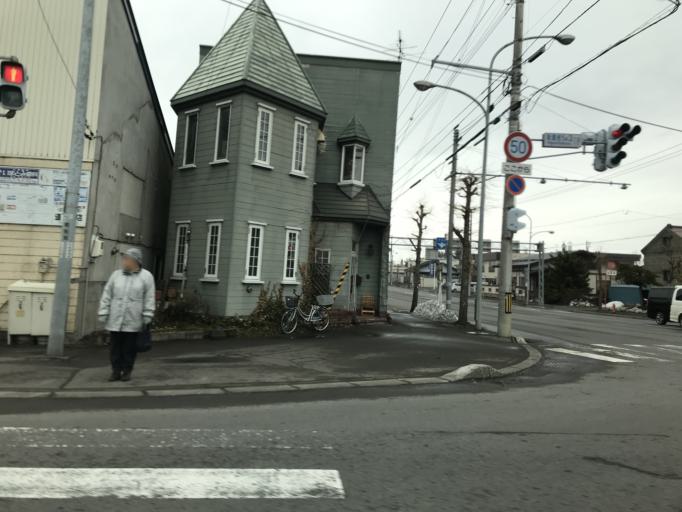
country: JP
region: Hokkaido
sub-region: Asahikawa-shi
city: Asahikawa
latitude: 43.8255
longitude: 142.4169
